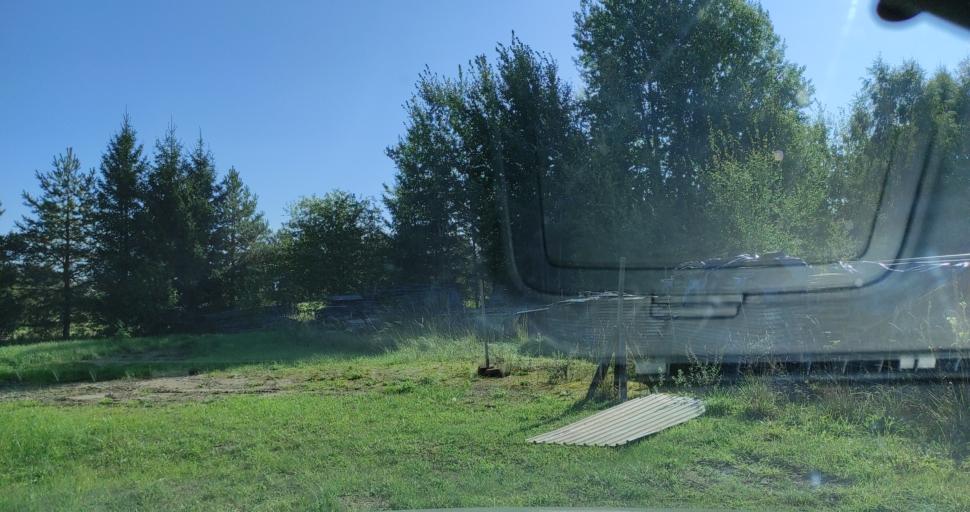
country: LV
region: Kuldigas Rajons
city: Kuldiga
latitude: 56.9731
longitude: 21.9223
